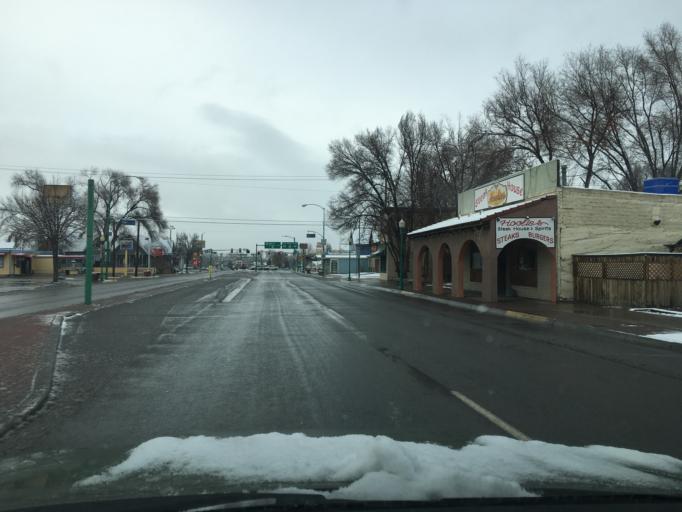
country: US
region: Colorado
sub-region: Delta County
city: Delta
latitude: 38.7436
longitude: -108.0708
